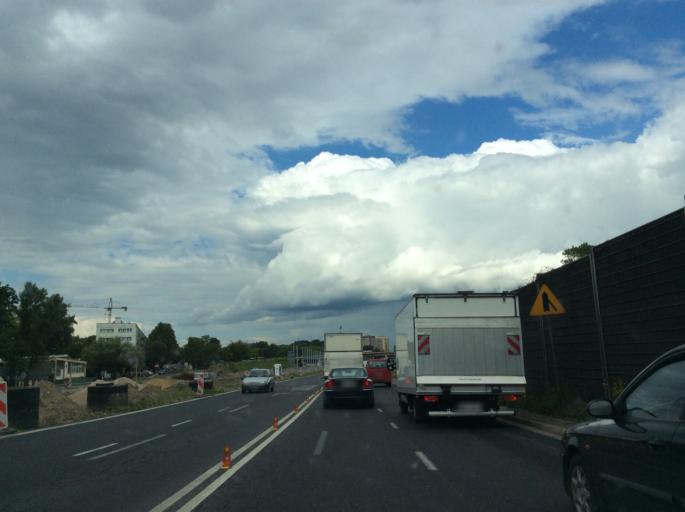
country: PL
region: Masovian Voivodeship
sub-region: Warszawa
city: Zoliborz
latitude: 52.2695
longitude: 20.9616
